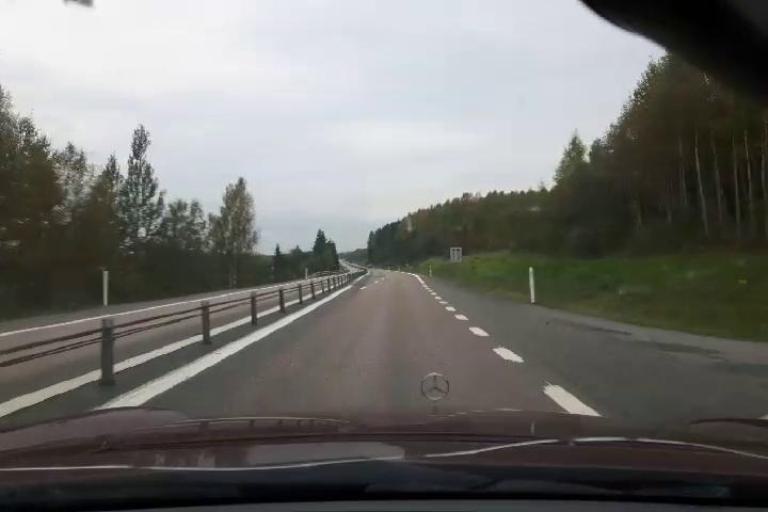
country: SE
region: Vaesternorrland
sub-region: Haernoesands Kommun
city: Haernoesand
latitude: 62.8526
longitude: 18.0100
